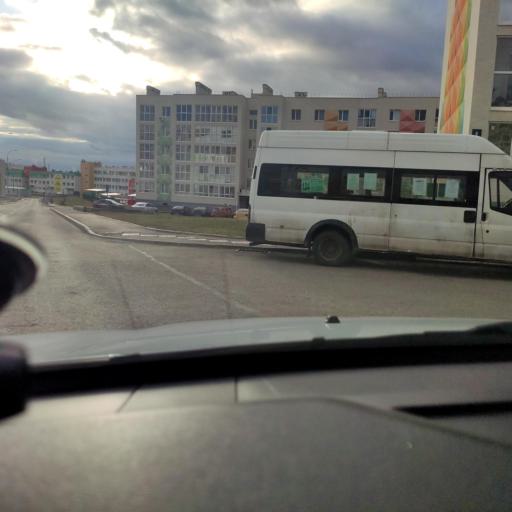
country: RU
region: Samara
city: Petra-Dubrava
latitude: 53.3015
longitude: 50.3339
